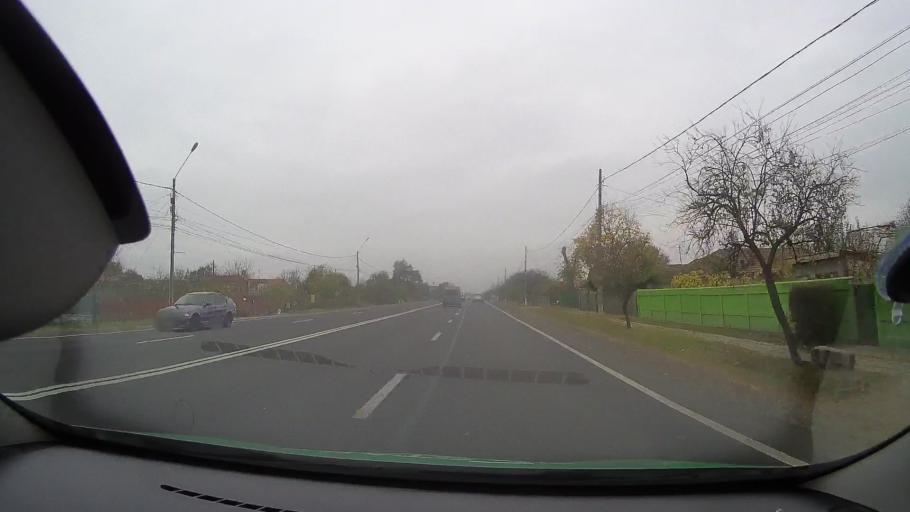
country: RO
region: Ilfov
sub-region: Comuna Ciolpani
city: Ciolpani
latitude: 44.7246
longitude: 26.1074
